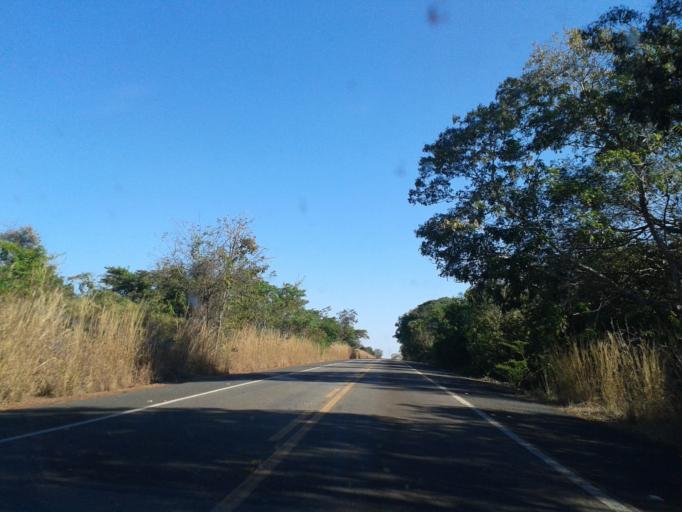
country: BR
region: Goias
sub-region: Mozarlandia
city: Mozarlandia
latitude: -15.0469
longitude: -50.6078
